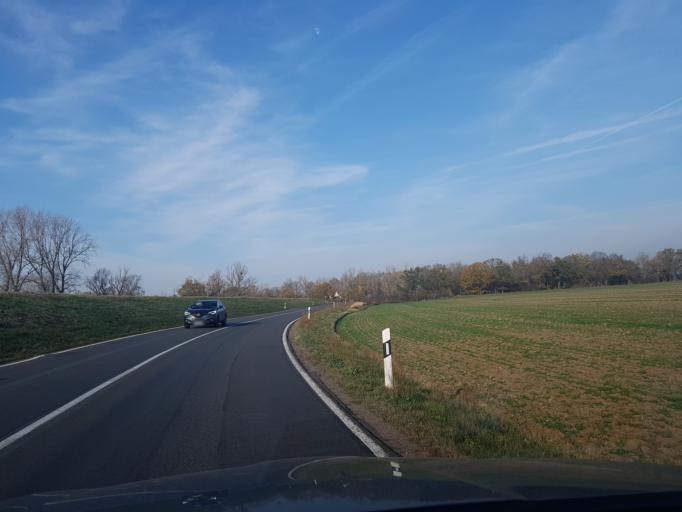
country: DE
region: Saxony
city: Beilrode
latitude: 51.5507
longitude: 13.0445
